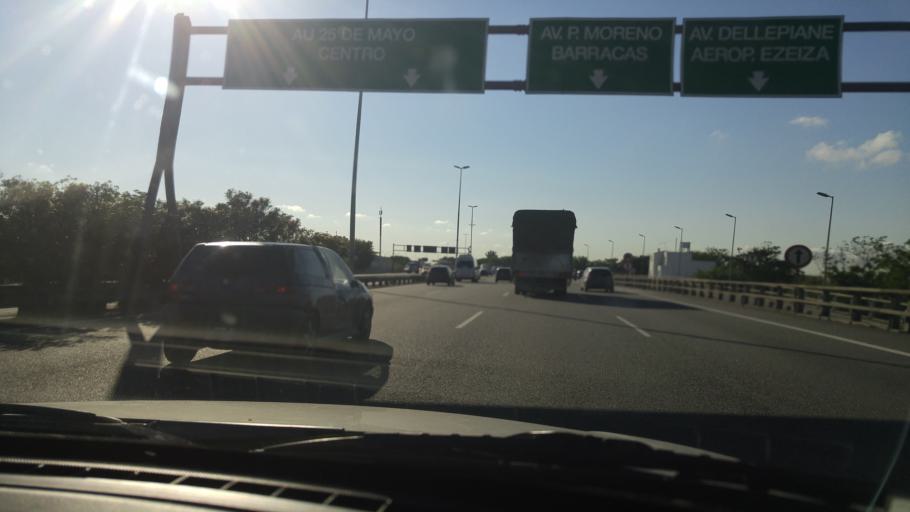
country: AR
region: Buenos Aires F.D.
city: Villa Santa Rita
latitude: -34.6436
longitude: -58.4893
